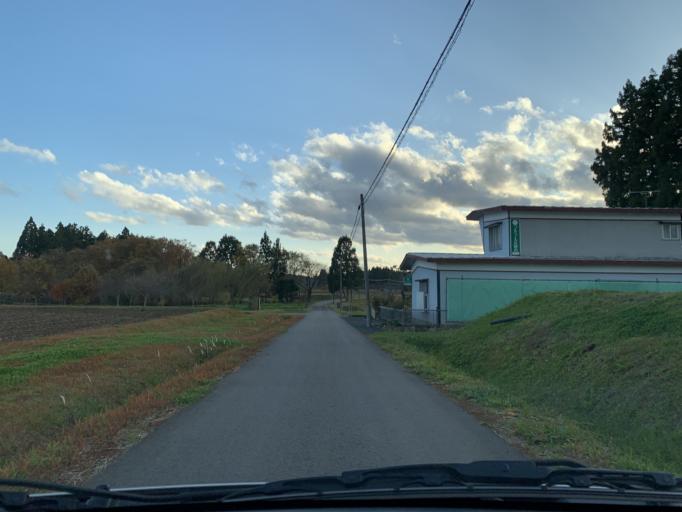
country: JP
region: Iwate
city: Mizusawa
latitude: 39.0875
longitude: 141.0363
